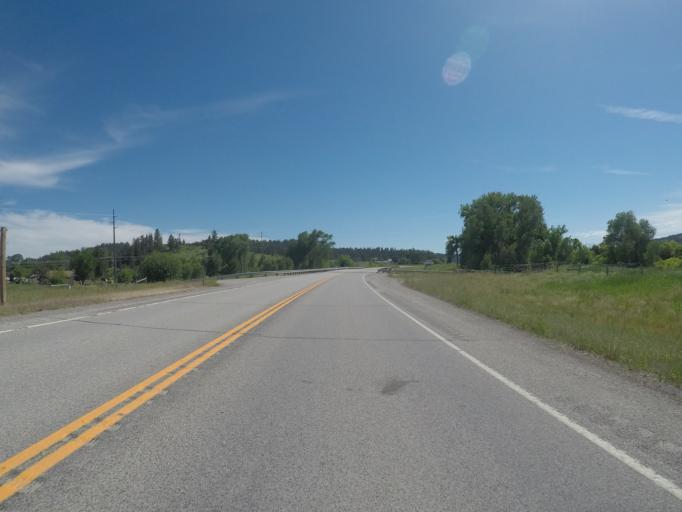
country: US
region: Montana
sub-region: Stillwater County
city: Columbus
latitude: 45.6136
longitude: -109.2797
